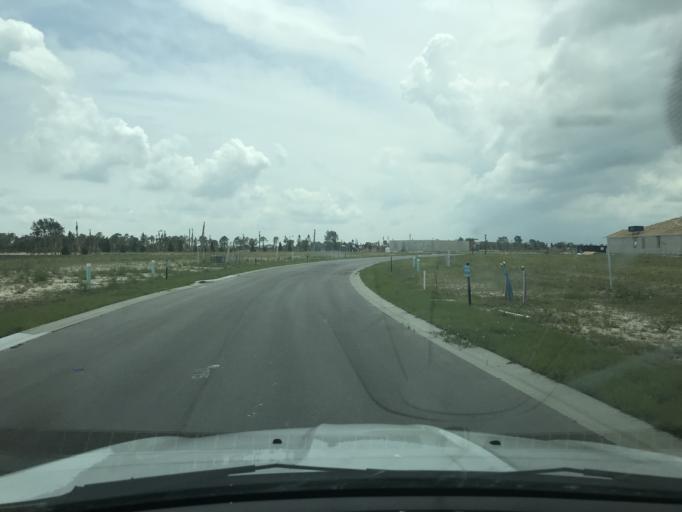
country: US
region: Florida
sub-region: Lee County
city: Olga
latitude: 26.7873
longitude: -81.7350
